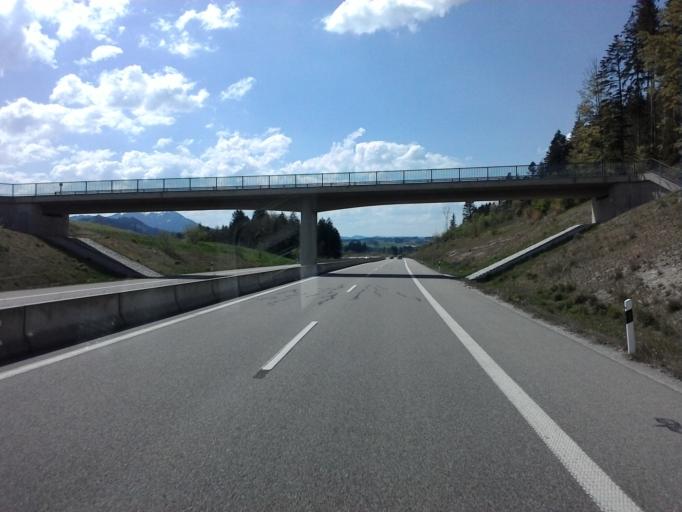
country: DE
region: Bavaria
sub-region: Swabia
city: Hopferau
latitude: 47.6262
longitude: 10.6365
